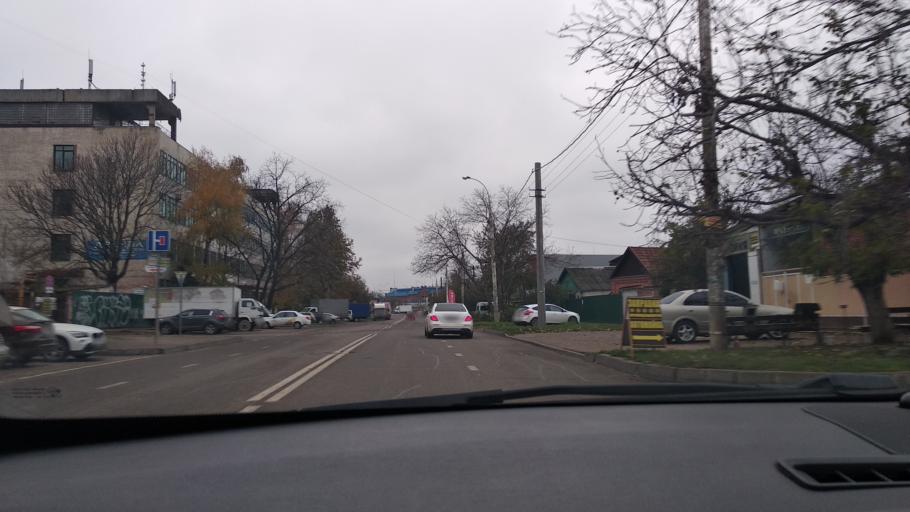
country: RU
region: Krasnodarskiy
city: Krasnodar
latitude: 45.0284
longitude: 39.0190
